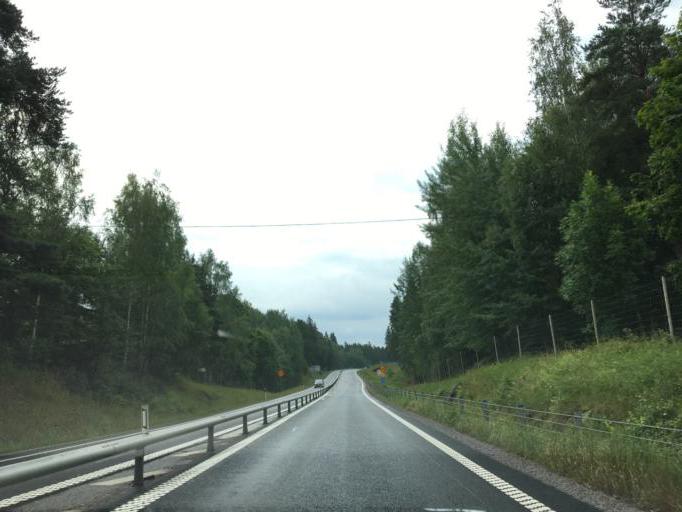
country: SE
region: Soedermanland
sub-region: Katrineholms Kommun
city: Katrineholm
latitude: 58.9040
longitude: 16.2030
